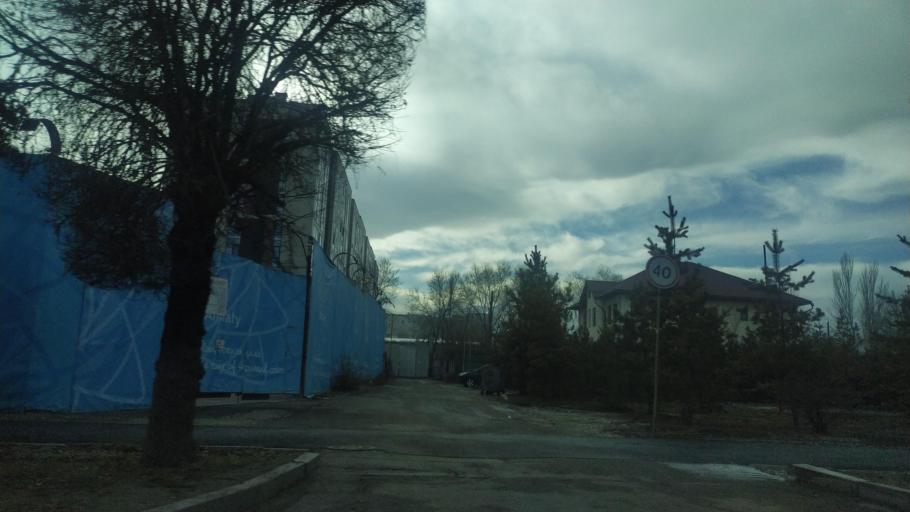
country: KZ
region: Almaty Qalasy
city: Almaty
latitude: 43.2379
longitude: 76.8876
